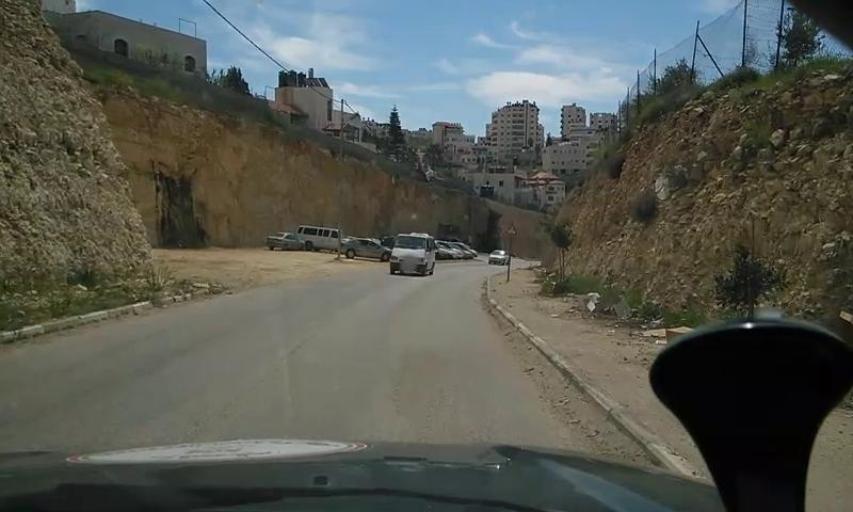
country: PS
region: West Bank
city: Bir Nabala
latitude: 31.8530
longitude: 35.2019
